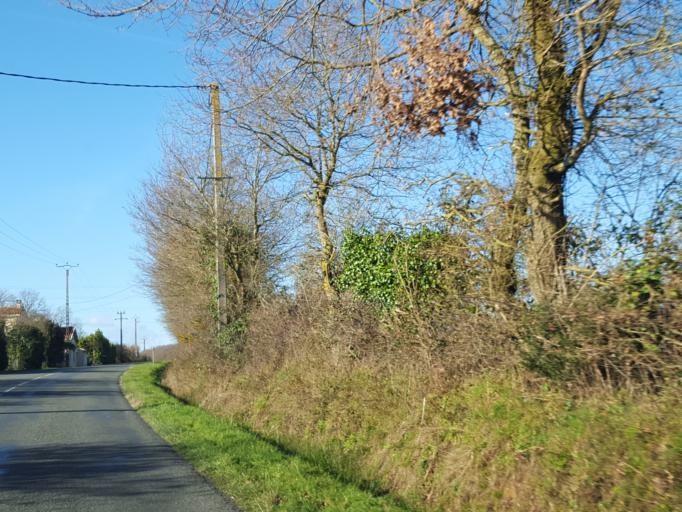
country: FR
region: Pays de la Loire
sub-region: Departement de la Vendee
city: La Roche-sur-Yon
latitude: 46.6704
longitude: -1.4734
